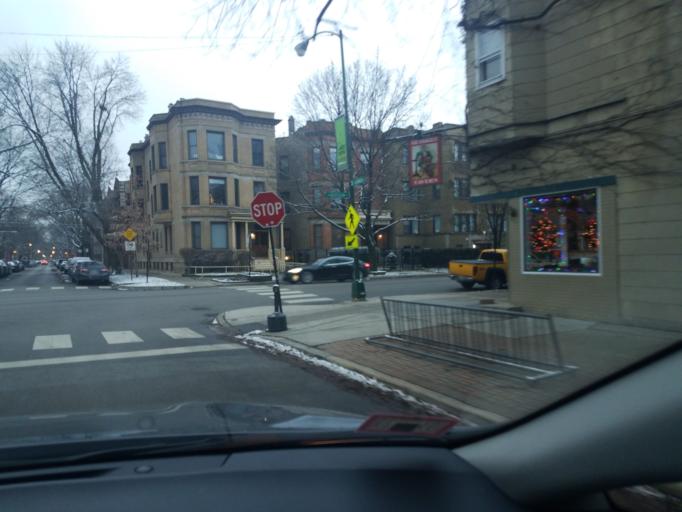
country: US
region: Illinois
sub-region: Cook County
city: Lincolnwood
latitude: 41.9474
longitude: -87.6617
